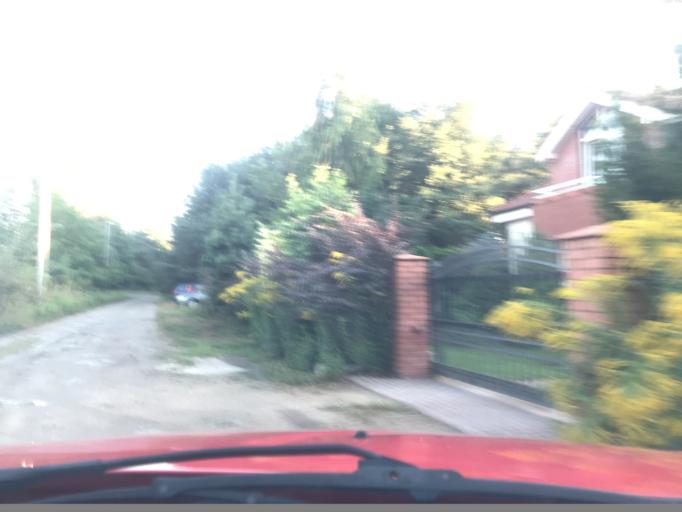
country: PL
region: Greater Poland Voivodeship
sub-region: Powiat poznanski
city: Tarnowo Podgorne
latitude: 52.4223
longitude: 16.7170
